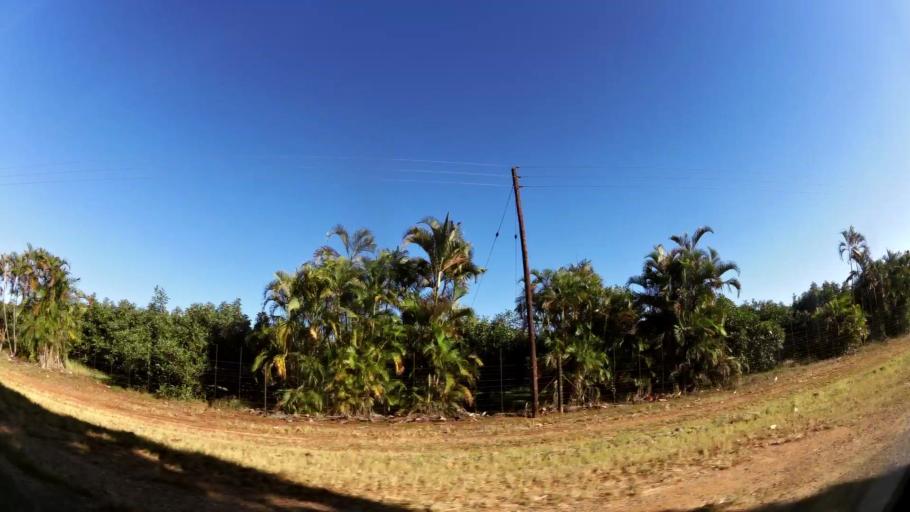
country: ZA
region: Limpopo
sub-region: Mopani District Municipality
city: Tzaneen
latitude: -23.8559
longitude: 30.1101
